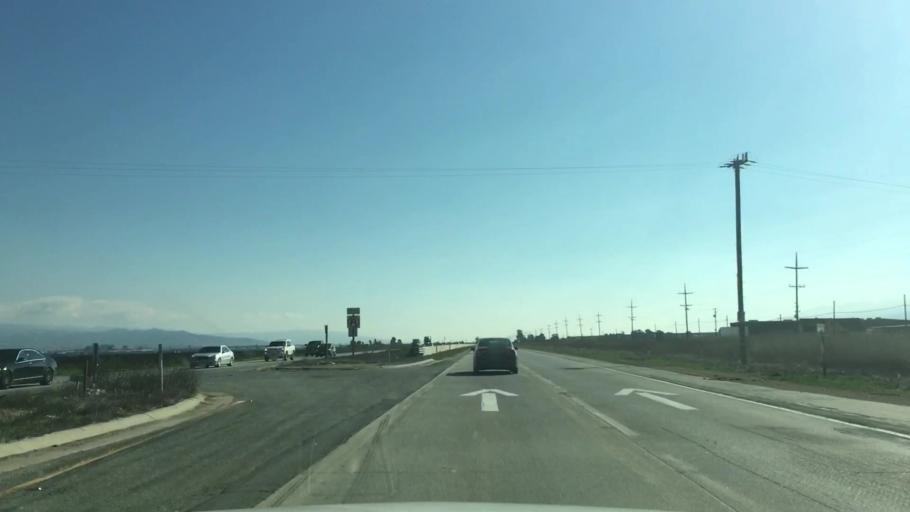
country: US
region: California
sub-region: Monterey County
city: Salinas
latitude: 36.6389
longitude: -121.6030
